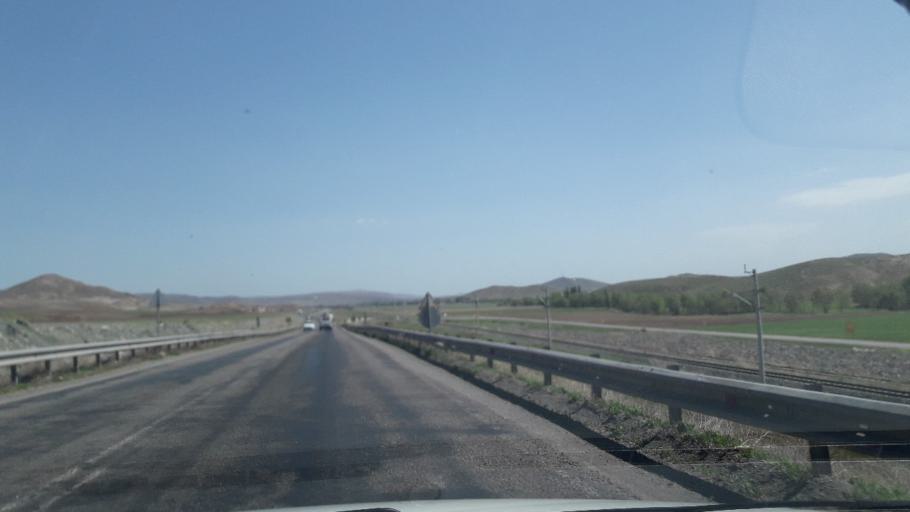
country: TR
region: Sivas
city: Ulas
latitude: 39.5223
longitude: 37.0101
